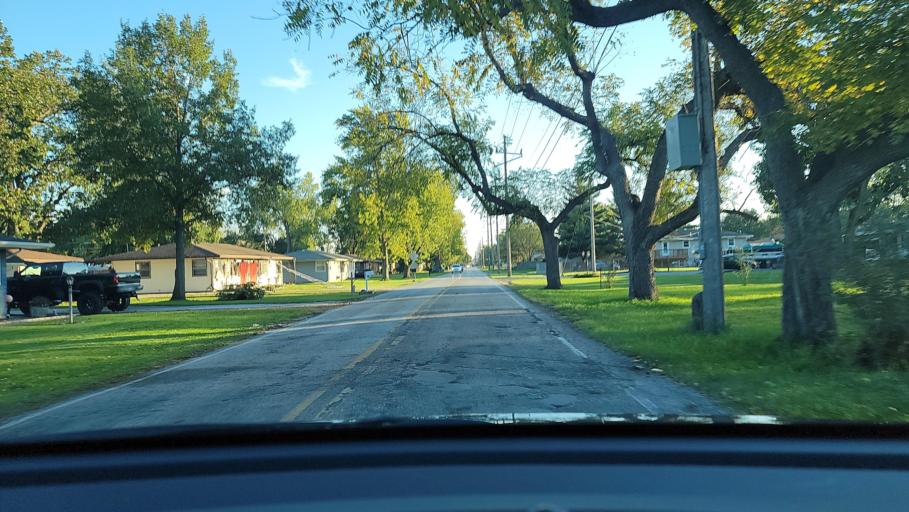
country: US
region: Indiana
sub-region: Porter County
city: Portage
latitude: 41.5645
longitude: -87.1975
